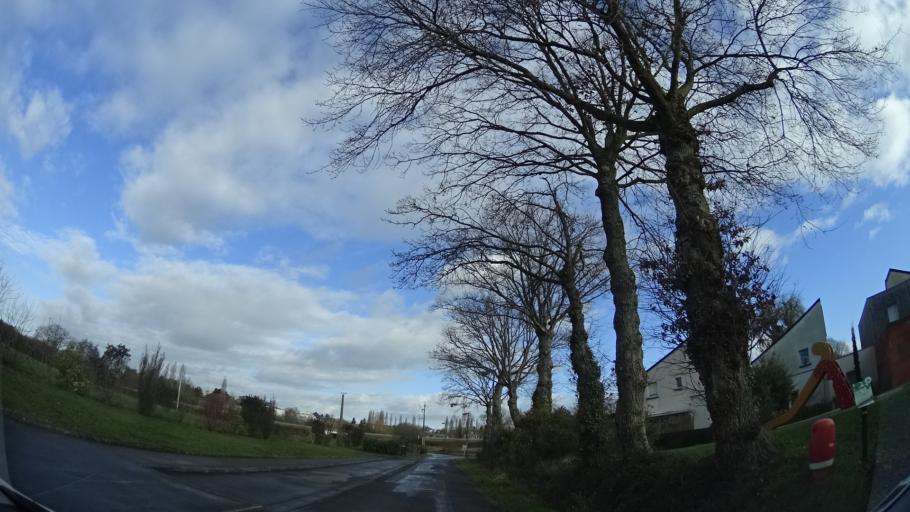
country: FR
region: Brittany
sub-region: Departement d'Ille-et-Vilaine
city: Chantepie
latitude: 48.0789
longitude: -1.6096
